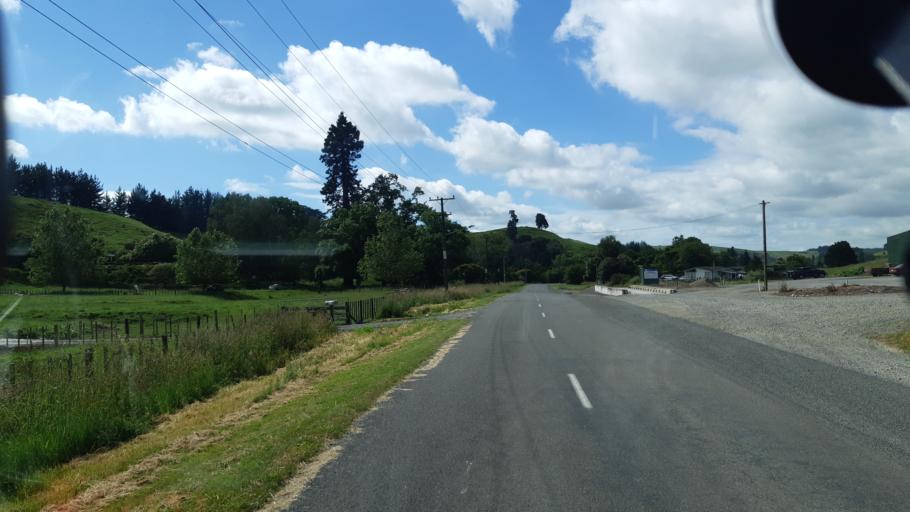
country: NZ
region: Manawatu-Wanganui
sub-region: Rangitikei District
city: Bulls
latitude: -39.9266
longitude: 175.5621
